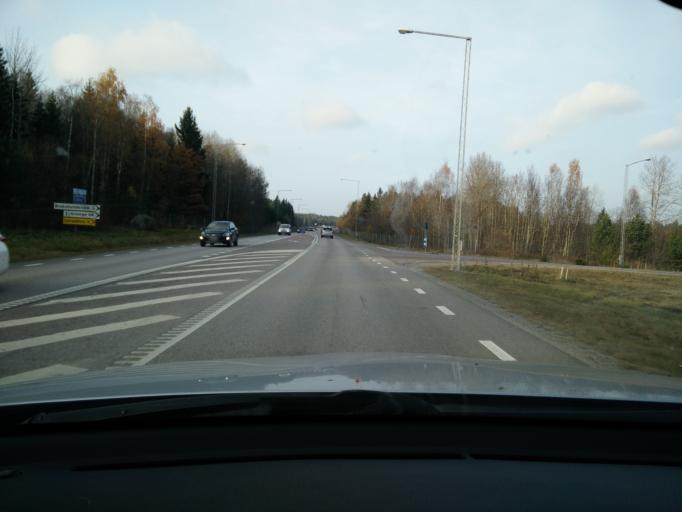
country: SE
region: Stockholm
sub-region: Taby Kommun
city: Taby
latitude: 59.4823
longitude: 18.1171
